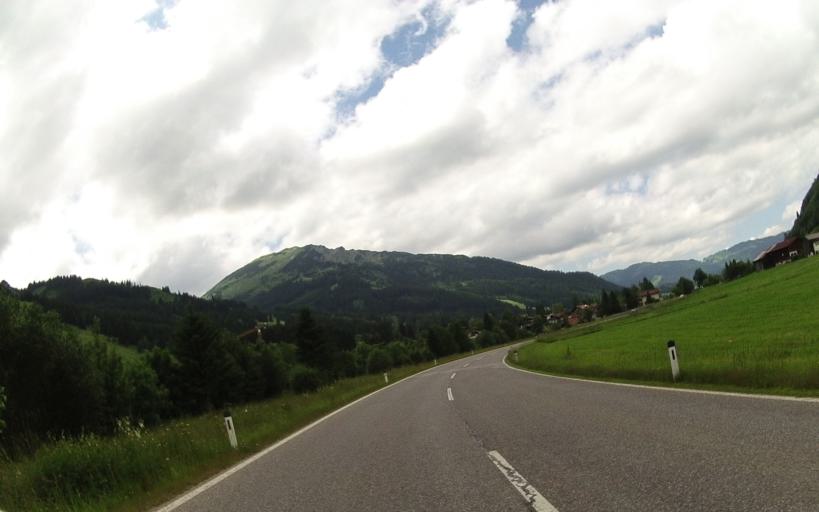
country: AT
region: Tyrol
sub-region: Politischer Bezirk Reutte
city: Zoblen
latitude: 47.5064
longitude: 10.4783
